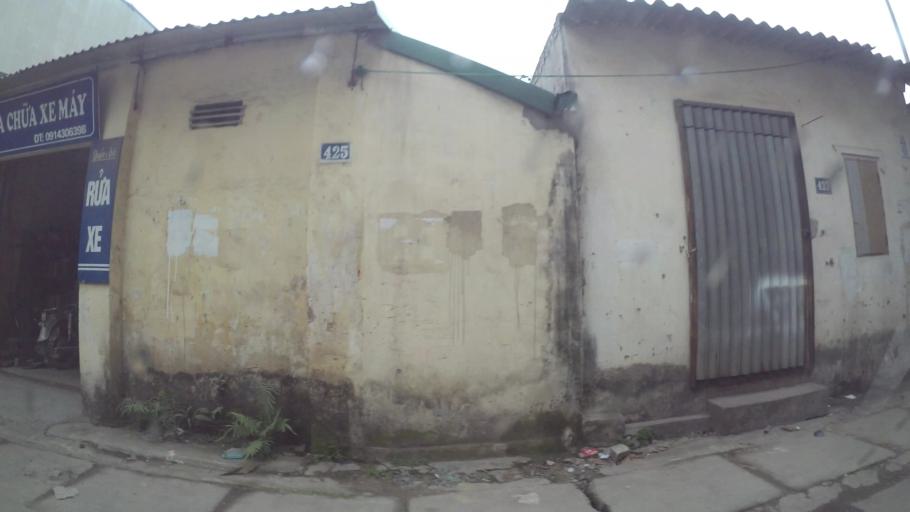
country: VN
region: Ha Noi
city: Van Dien
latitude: 20.9766
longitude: 105.8857
